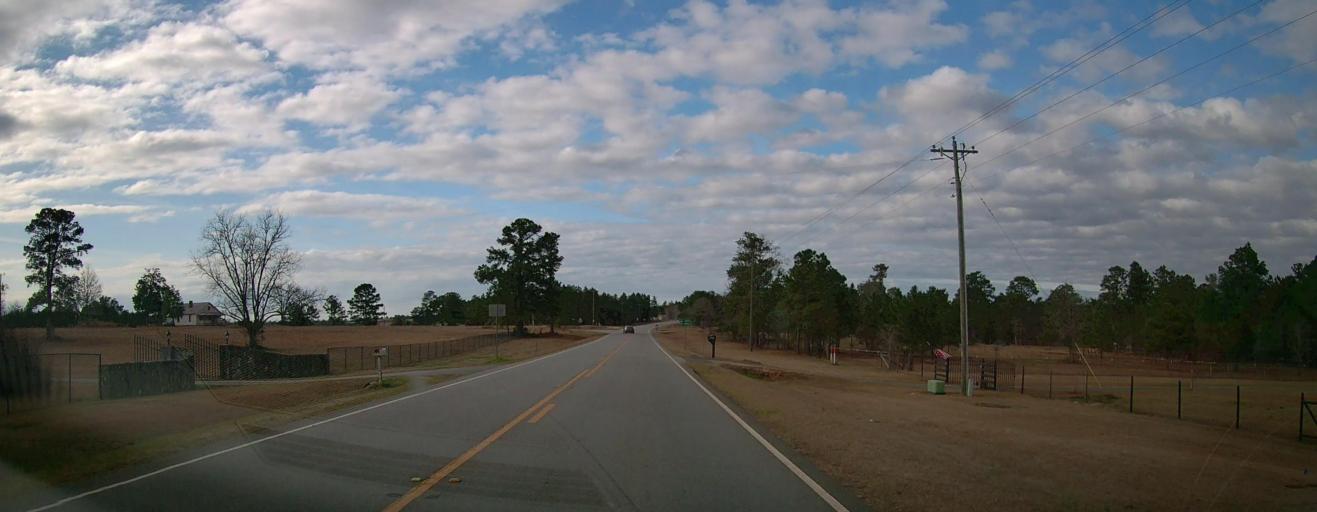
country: US
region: Georgia
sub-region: Marion County
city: Buena Vista
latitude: 32.4917
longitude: -84.5532
